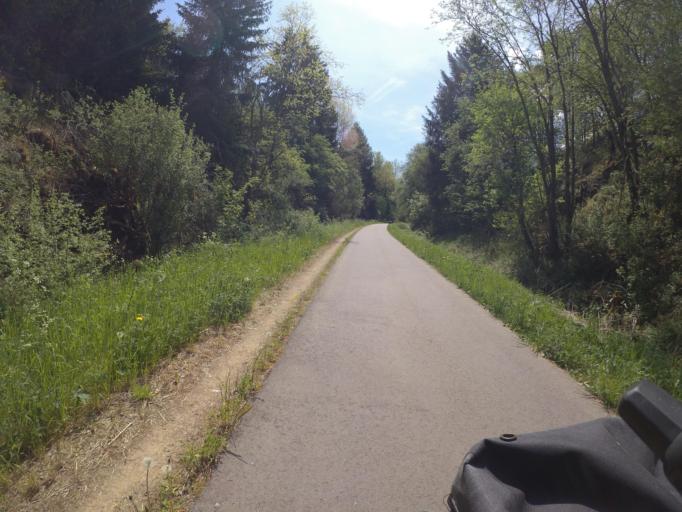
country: BE
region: Wallonia
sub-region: Province de Liege
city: Bullange
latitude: 50.4201
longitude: 6.2525
